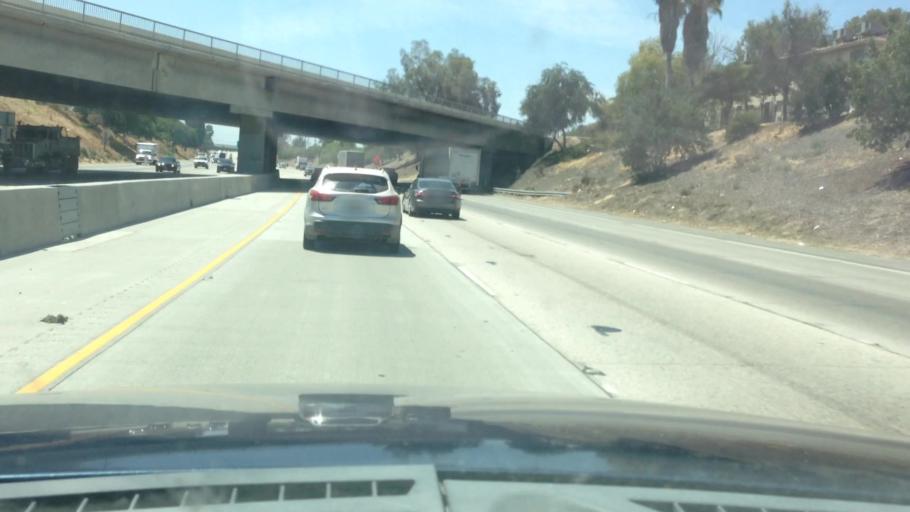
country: US
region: California
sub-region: Kern County
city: Bakersfield
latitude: 35.3310
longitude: -119.0396
